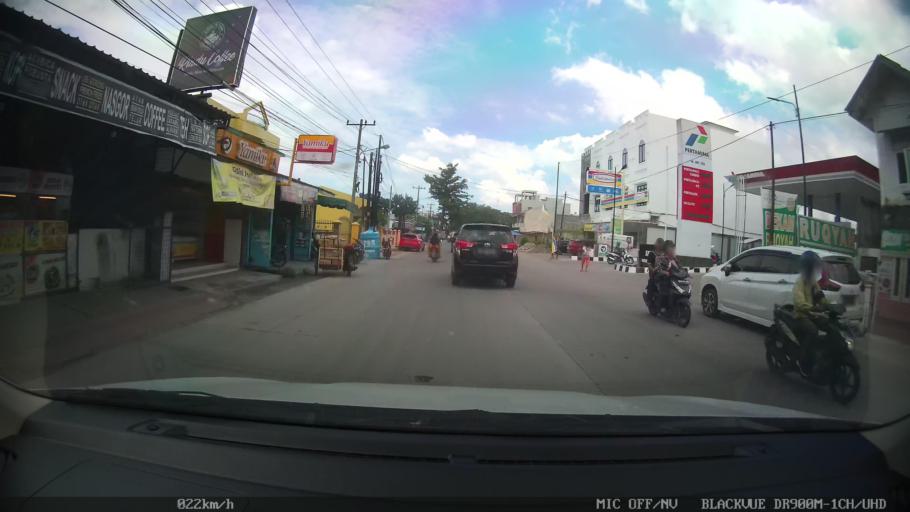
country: ID
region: North Sumatra
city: Sunggal
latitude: 3.6054
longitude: 98.6250
